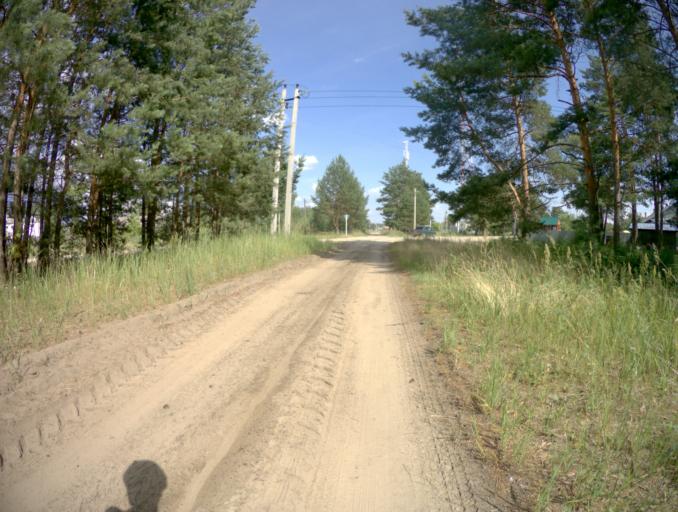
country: RU
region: Ivanovo
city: Talitsy
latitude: 56.5311
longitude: 42.3204
